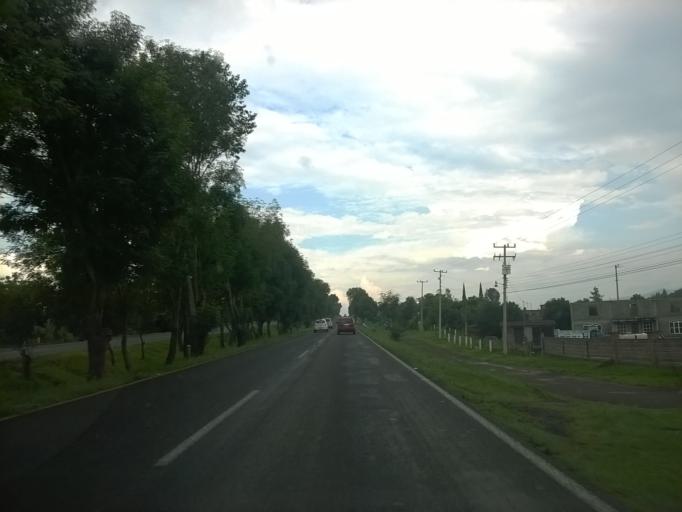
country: MX
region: Michoacan
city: Cuanajo
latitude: 19.5352
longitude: -101.5105
